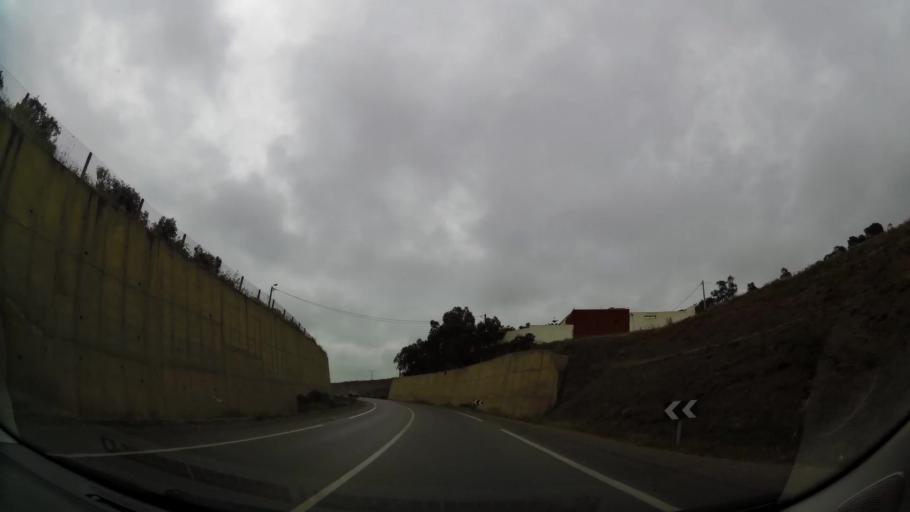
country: MA
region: Oriental
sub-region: Nador
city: Nador
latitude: 35.1530
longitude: -3.0206
